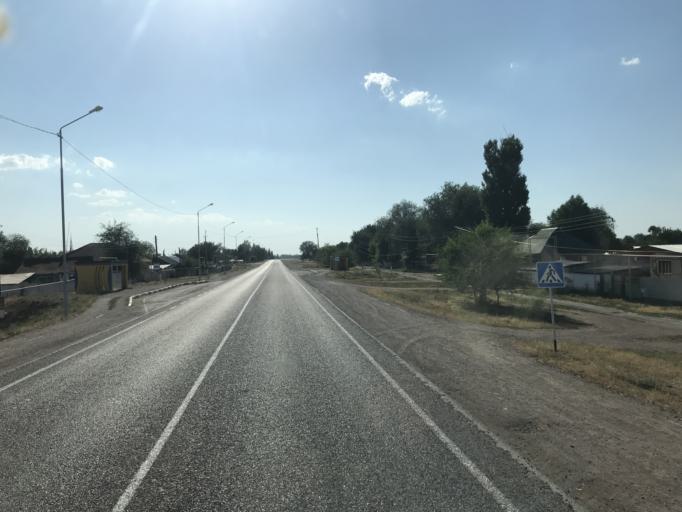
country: KZ
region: Zhambyl
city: Georgiyevka
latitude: 43.2275
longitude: 74.3923
